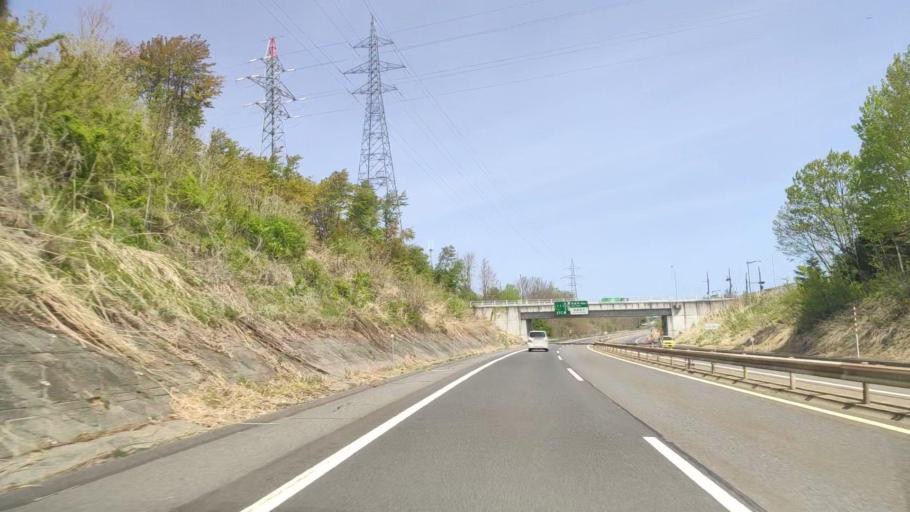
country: JP
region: Aomori
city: Hachinohe
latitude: 40.4808
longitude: 141.4596
